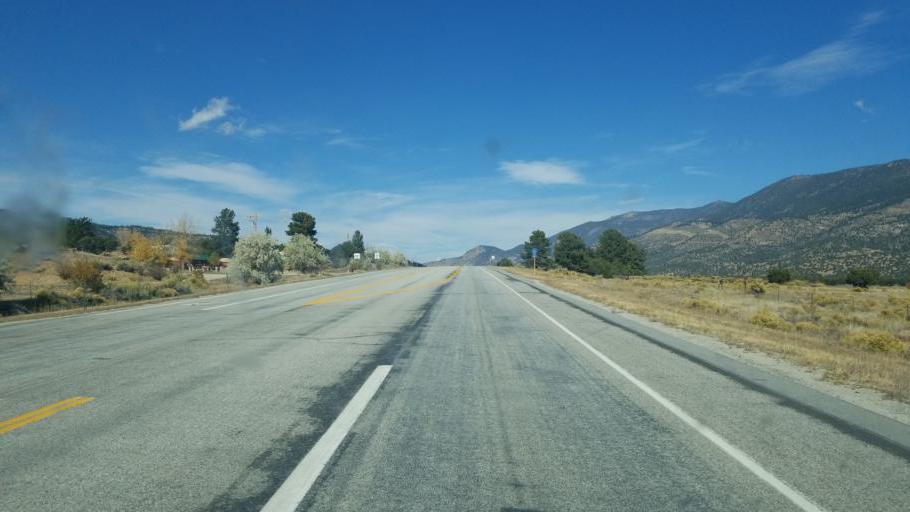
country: US
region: Colorado
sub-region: Chaffee County
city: Buena Vista
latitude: 38.9101
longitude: -106.1793
